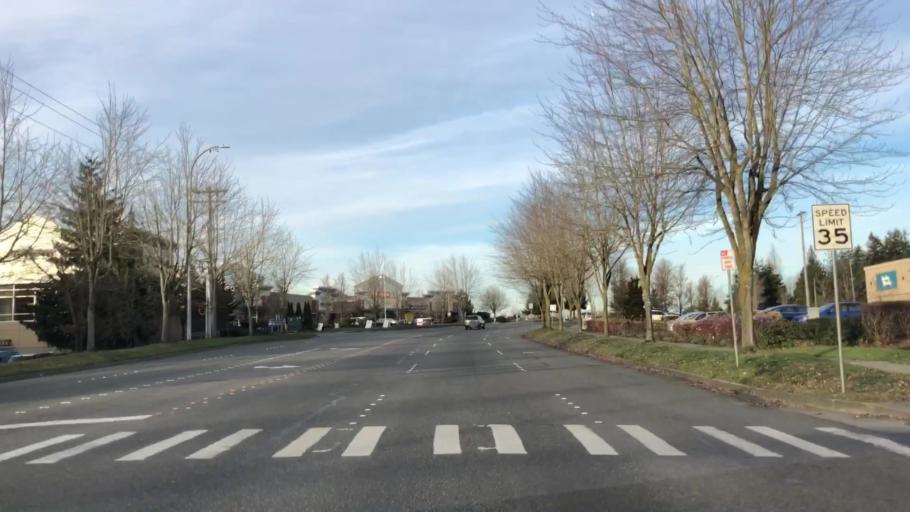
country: US
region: Washington
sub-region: Snohomish County
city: Alderwood Manor
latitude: 47.8227
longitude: -122.2710
